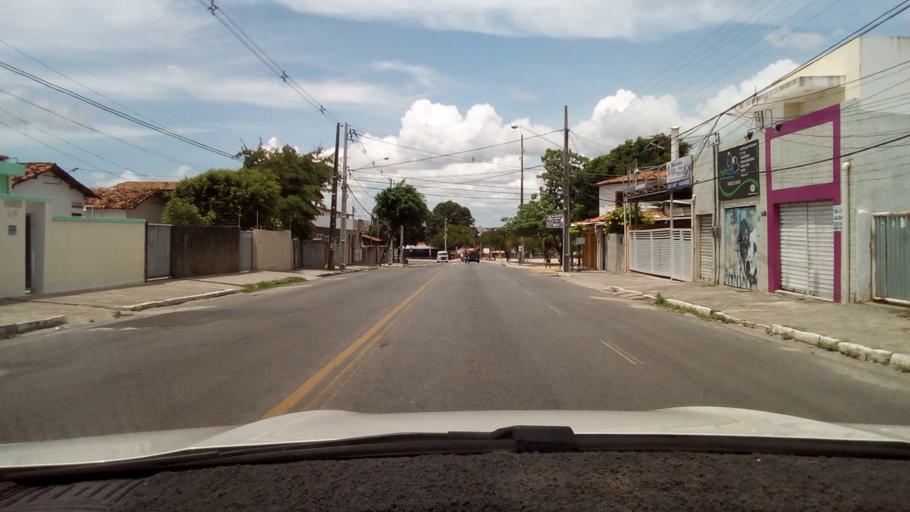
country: BR
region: Paraiba
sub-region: Joao Pessoa
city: Joao Pessoa
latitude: -7.1731
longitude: -34.8438
